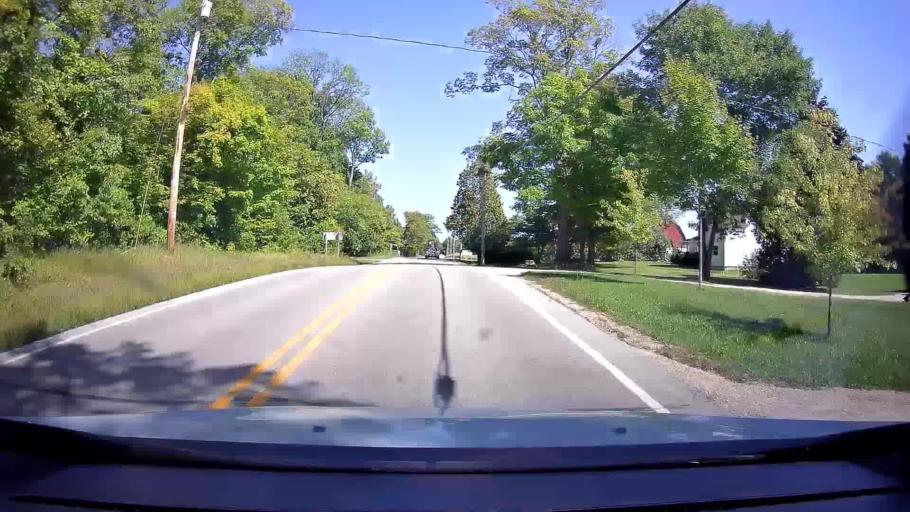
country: US
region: Michigan
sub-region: Delta County
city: Escanaba
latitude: 45.2891
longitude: -87.0145
